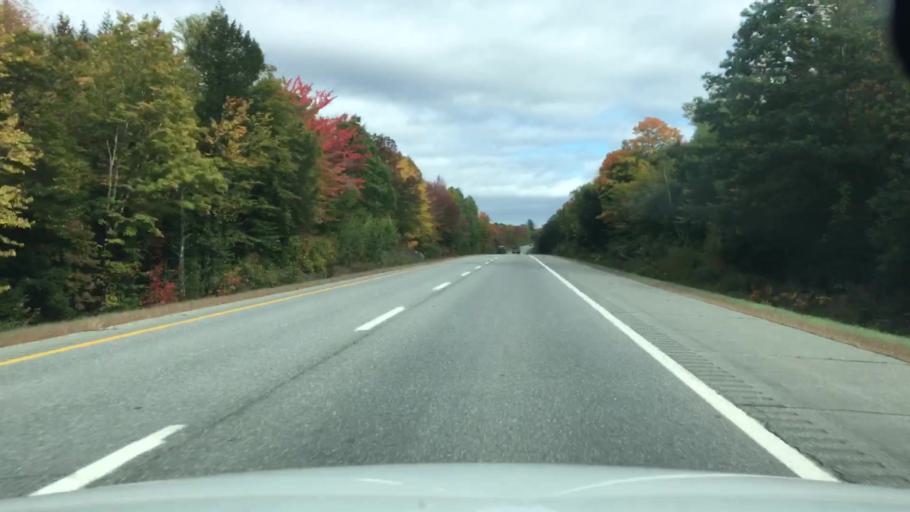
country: US
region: Maine
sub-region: Penobscot County
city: Carmel
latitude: 44.7734
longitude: -69.0227
